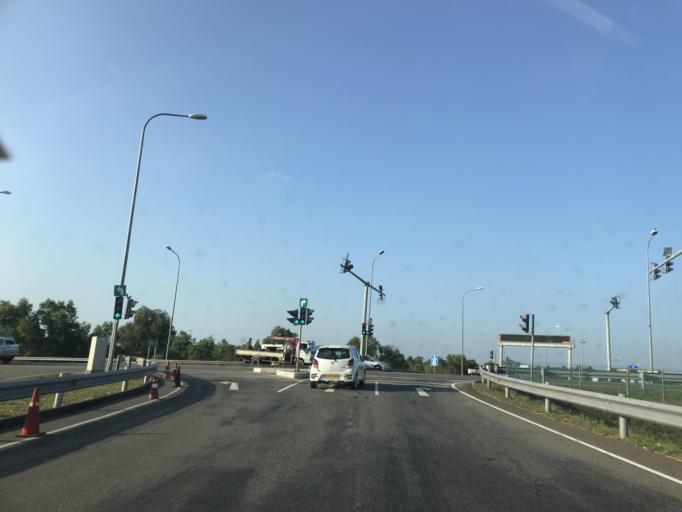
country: LK
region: Western
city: Ja Ela
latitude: 7.0812
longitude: 79.8769
